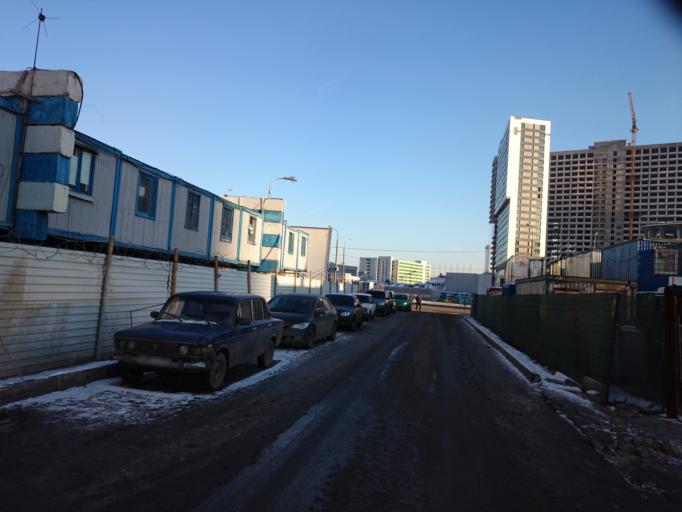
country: RU
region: Moscow
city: Sokol
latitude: 55.7880
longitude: 37.5380
